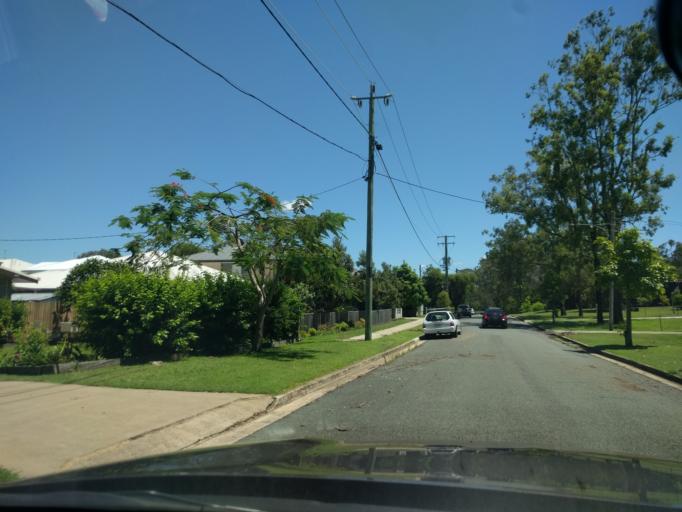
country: AU
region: Queensland
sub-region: Logan
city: Cedar Vale
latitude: -27.9873
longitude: 153.0071
